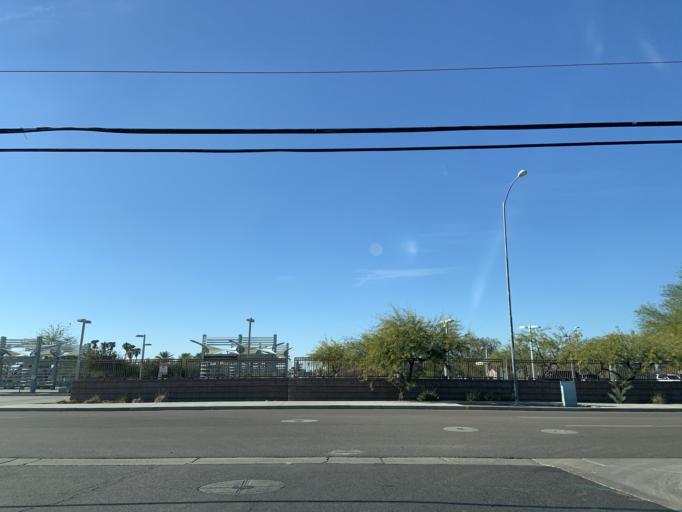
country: US
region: Arizona
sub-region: Maricopa County
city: Tempe
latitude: 33.4160
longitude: -111.8698
